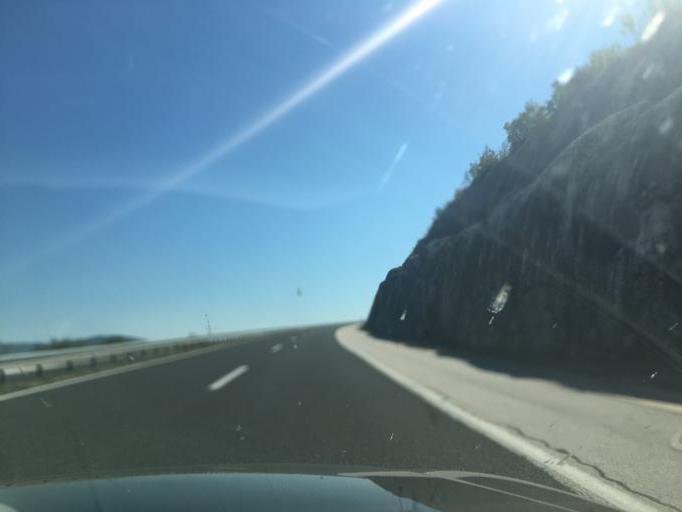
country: HR
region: Splitsko-Dalmatinska
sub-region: Grad Trogir
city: Trogir
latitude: 43.6320
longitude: 16.2250
